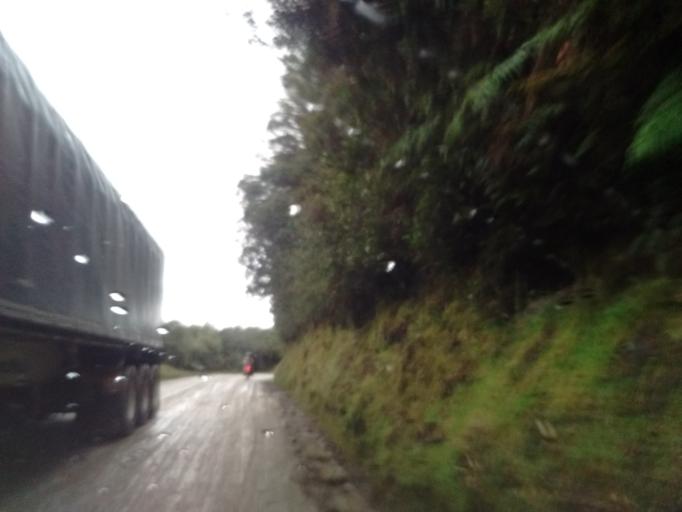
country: CO
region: Cauca
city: Paispamba
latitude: 2.1644
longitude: -76.4025
